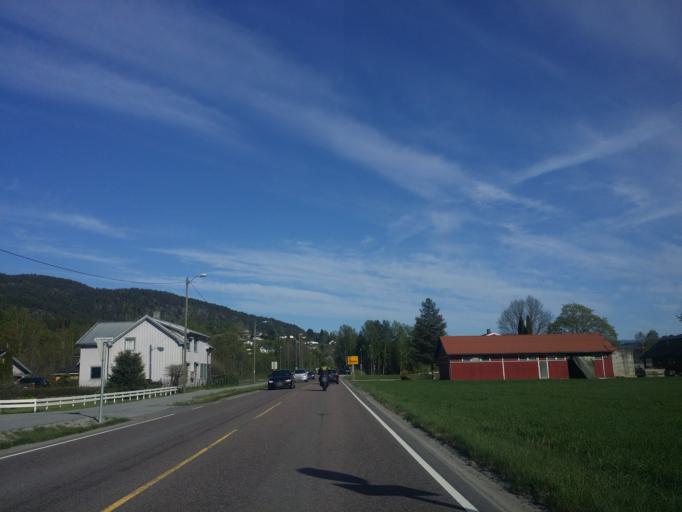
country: NO
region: Telemark
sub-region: Notodden
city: Notodden
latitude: 59.5771
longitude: 9.1865
